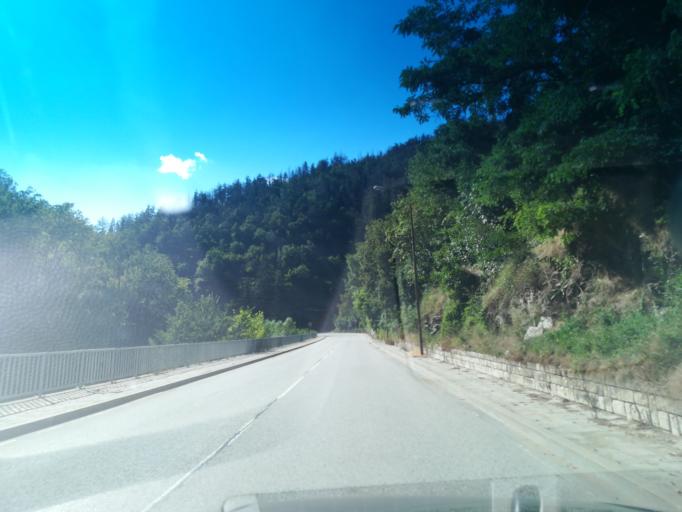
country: BG
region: Plovdiv
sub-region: Obshtina Luki
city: Luki
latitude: 41.8985
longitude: 24.7451
